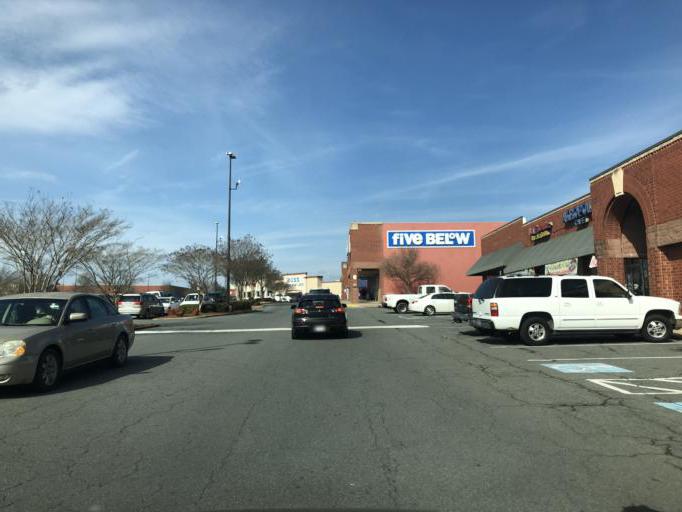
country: US
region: North Carolina
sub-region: Gaston County
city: Lowell
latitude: 35.2592
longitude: -81.1228
